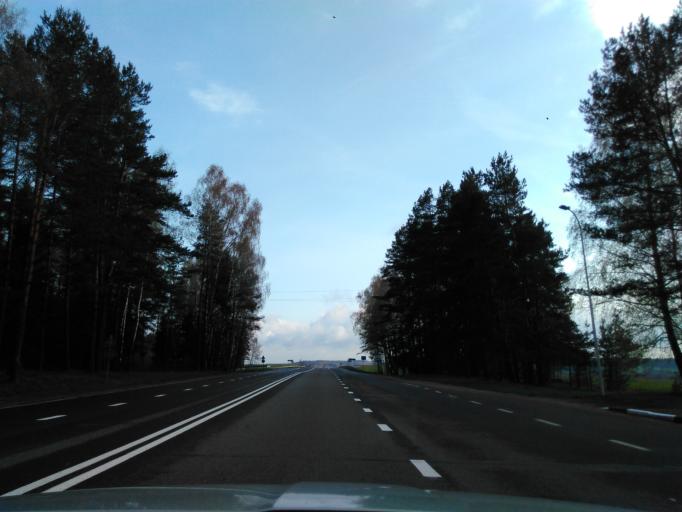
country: BY
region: Minsk
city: Lahoysk
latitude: 54.2426
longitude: 27.8429
